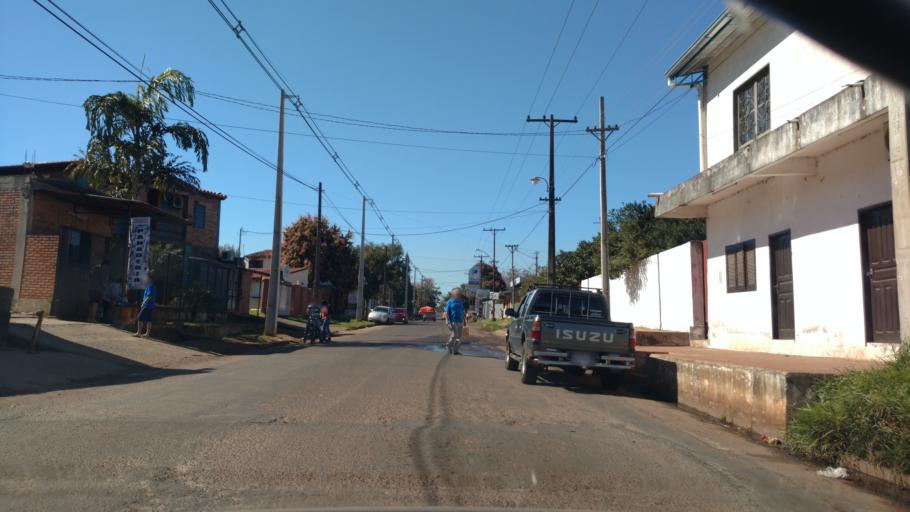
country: PY
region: Central
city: Itaugua
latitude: -25.3990
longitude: -57.3440
